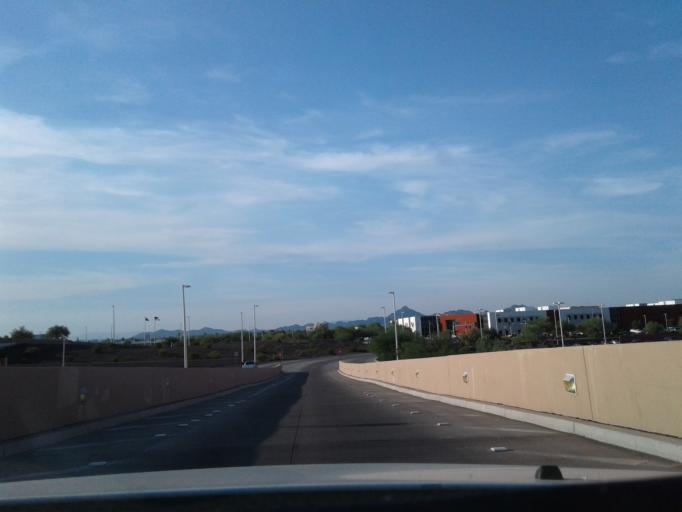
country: US
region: Arizona
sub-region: Maricopa County
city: Phoenix
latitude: 33.4294
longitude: -112.0426
